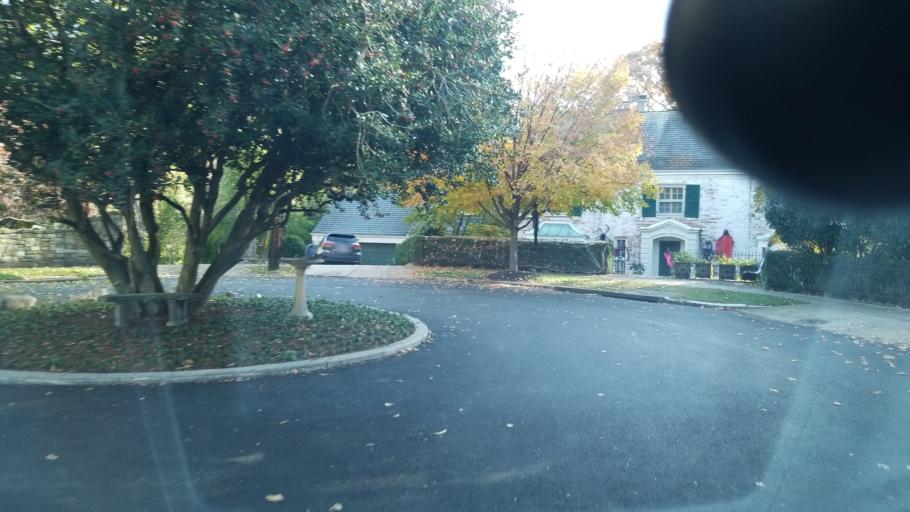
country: US
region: Maryland
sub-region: Montgomery County
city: Chevy Chase
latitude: 38.9509
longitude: -77.0551
